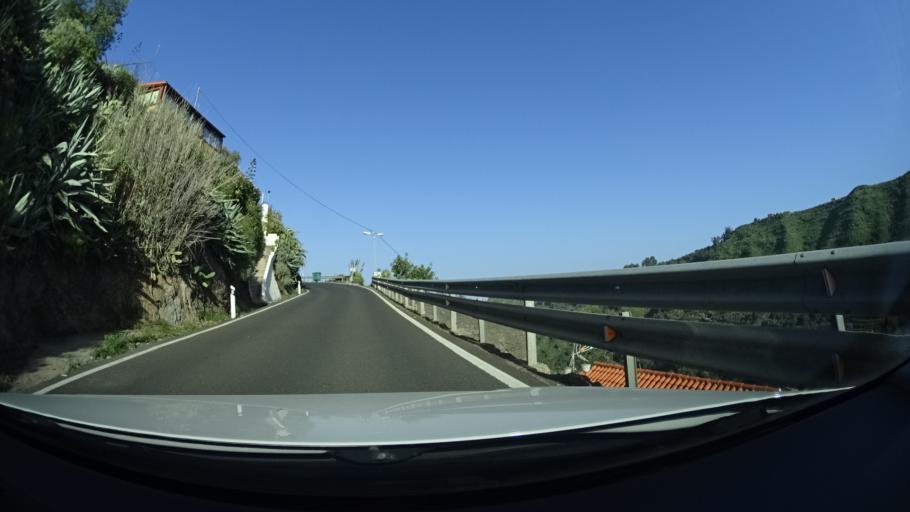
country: ES
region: Canary Islands
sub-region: Provincia de Las Palmas
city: Vega de San Mateo
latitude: 28.0205
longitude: -15.5510
